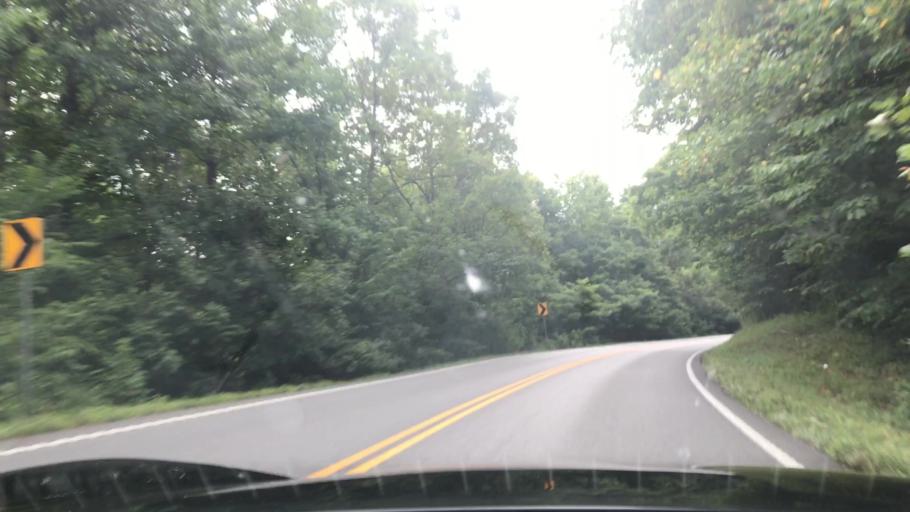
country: US
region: Kentucky
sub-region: Muhlenberg County
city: Central City
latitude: 37.2048
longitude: -87.0376
